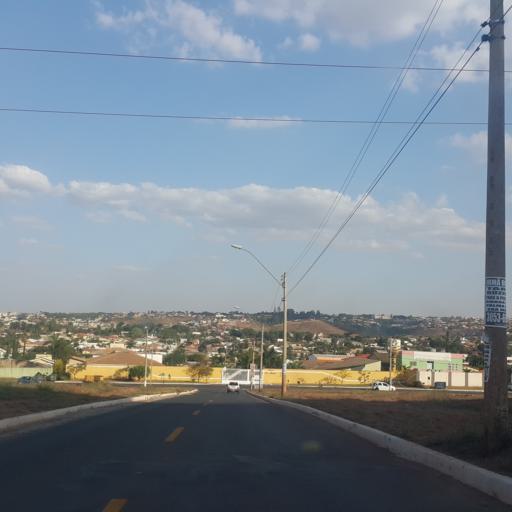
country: BR
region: Federal District
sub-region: Brasilia
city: Brasilia
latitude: -15.8407
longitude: -48.0131
